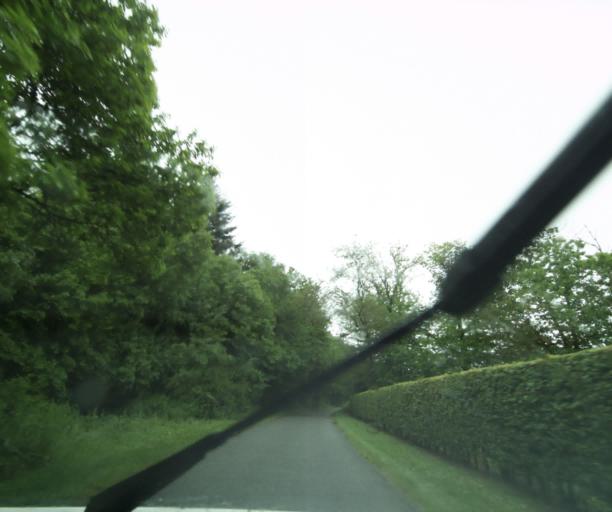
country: FR
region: Bourgogne
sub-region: Departement de Saone-et-Loire
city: Ciry-le-Noble
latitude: 46.5413
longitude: 4.3023
